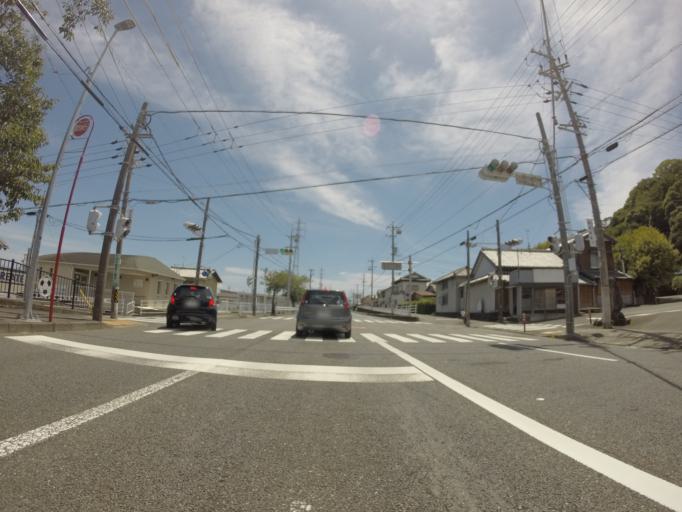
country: JP
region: Shizuoka
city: Shizuoka-shi
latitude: 34.9929
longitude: 138.4840
